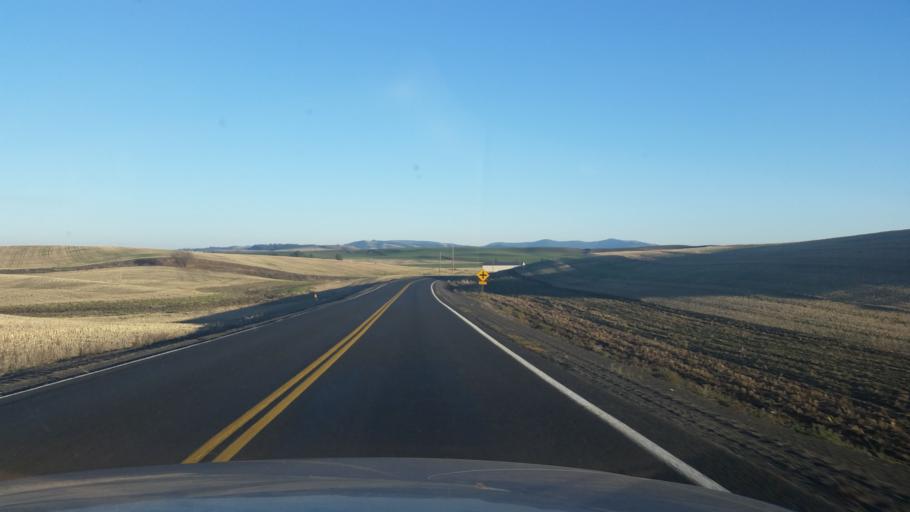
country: US
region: Washington
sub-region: Spokane County
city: Opportunity
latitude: 47.3686
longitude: -117.2953
